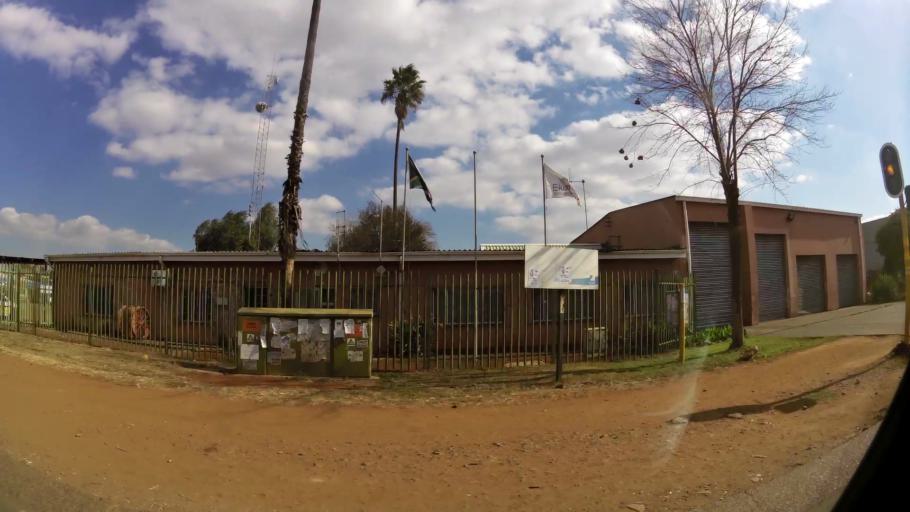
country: ZA
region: Gauteng
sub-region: Ekurhuleni Metropolitan Municipality
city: Tembisa
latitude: -25.9726
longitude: 28.2377
